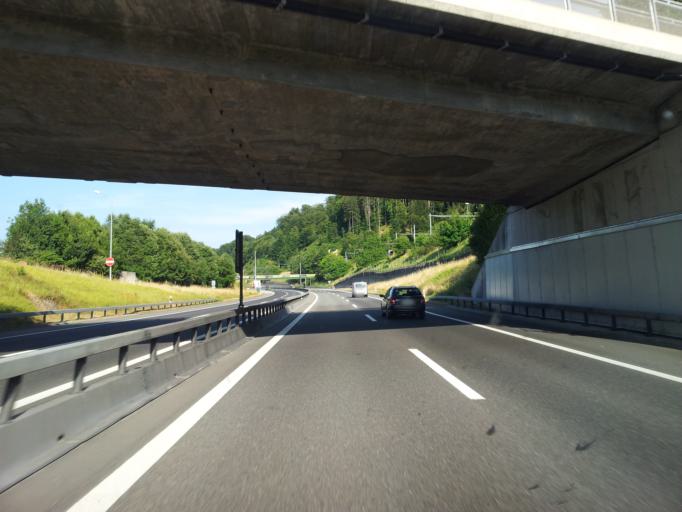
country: CH
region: Fribourg
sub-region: Sense District
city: Flamatt
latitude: 46.8887
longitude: 7.3233
